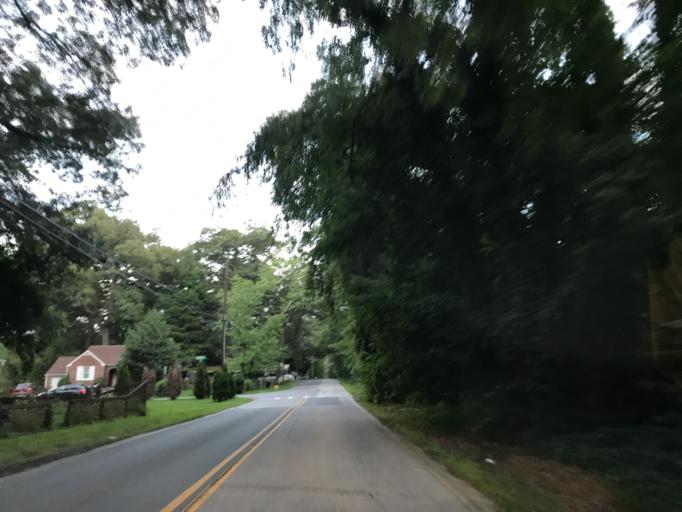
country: US
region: Maryland
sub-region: Anne Arundel County
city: Pasadena
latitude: 39.1063
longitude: -76.5751
